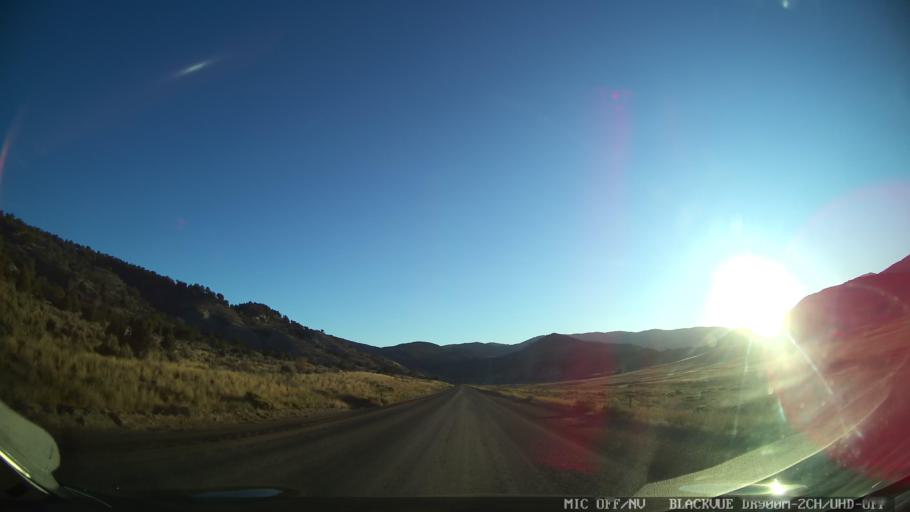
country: US
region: Colorado
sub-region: Grand County
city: Kremmling
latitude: 39.9205
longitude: -106.5424
